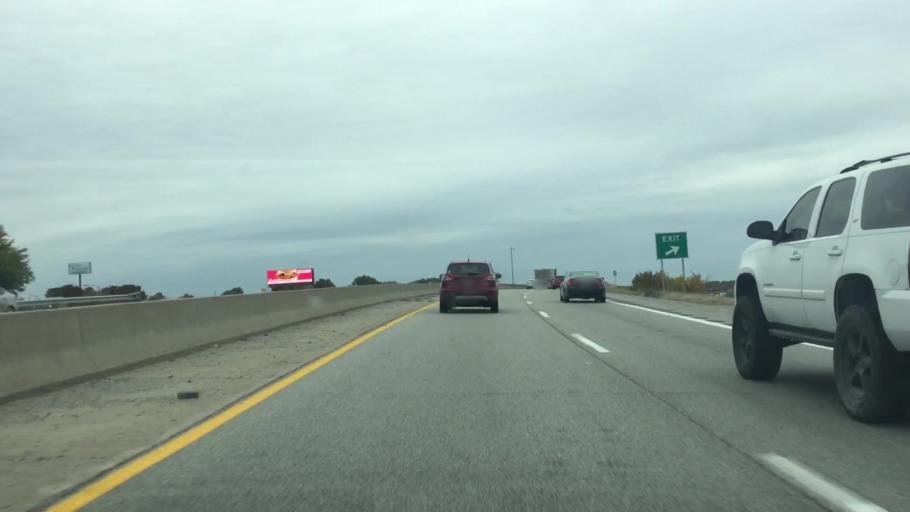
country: US
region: Missouri
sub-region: Jackson County
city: Lees Summit
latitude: 38.9096
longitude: -94.3914
